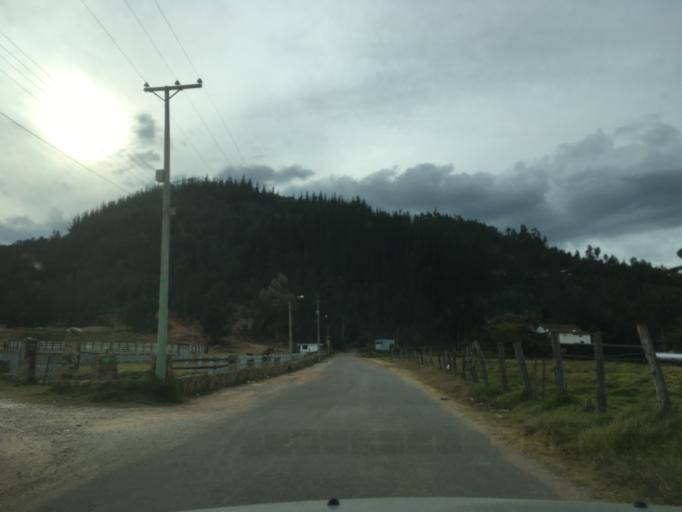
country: CO
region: Boyaca
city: Firavitoba
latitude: 5.6704
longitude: -72.9989
